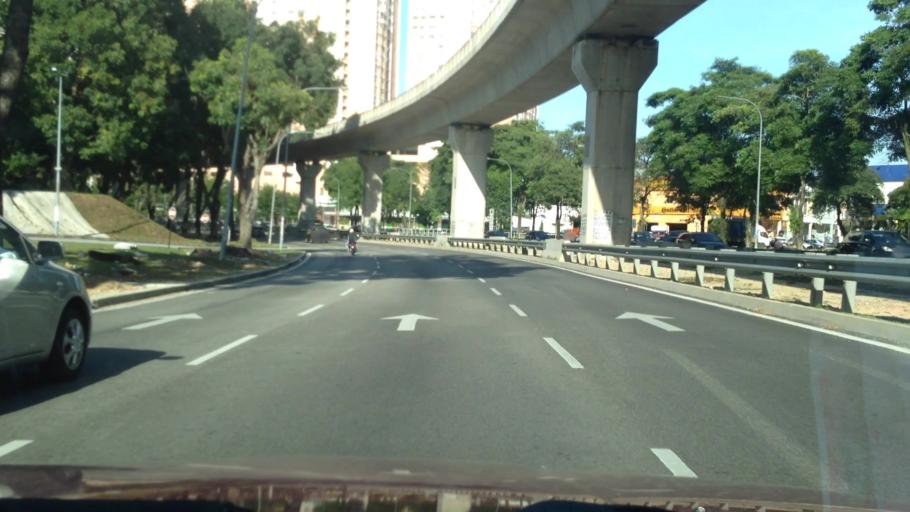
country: MY
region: Selangor
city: Subang Jaya
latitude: 3.0311
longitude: 101.5863
